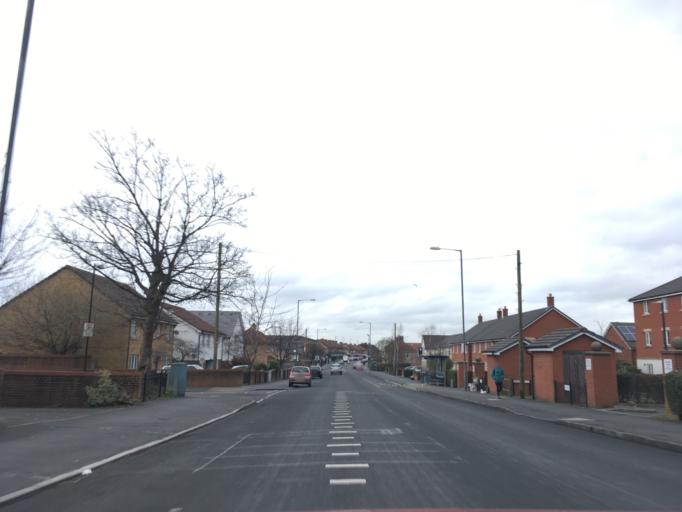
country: GB
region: England
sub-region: South Gloucestershire
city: Stoke Gifford
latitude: 51.4982
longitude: -2.5722
